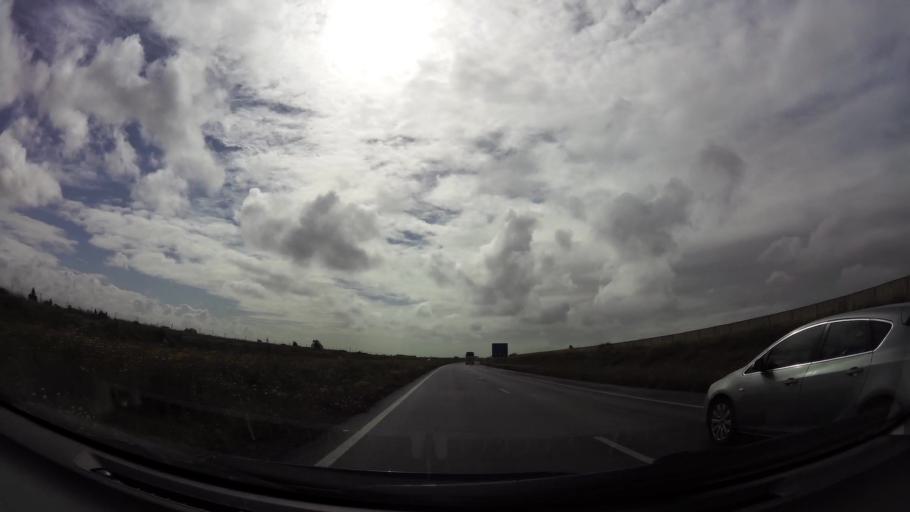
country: MA
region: Grand Casablanca
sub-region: Nouaceur
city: Dar Bouazza
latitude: 33.3539
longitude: -7.9628
